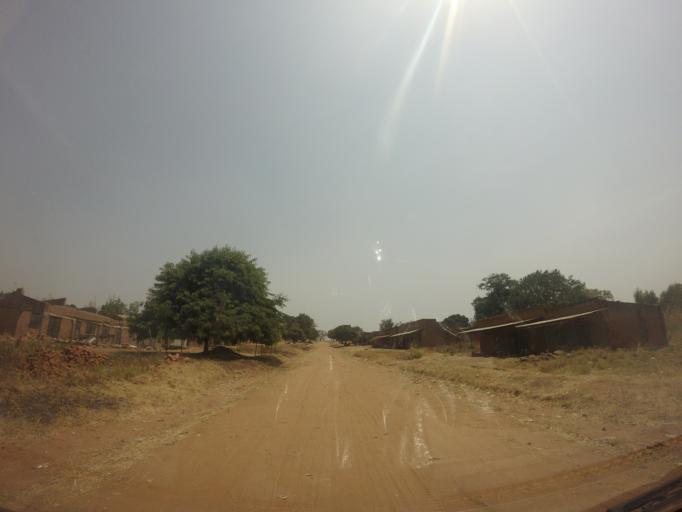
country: UG
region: Northern Region
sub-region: Arua District
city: Arua
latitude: 2.9156
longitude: 31.0252
